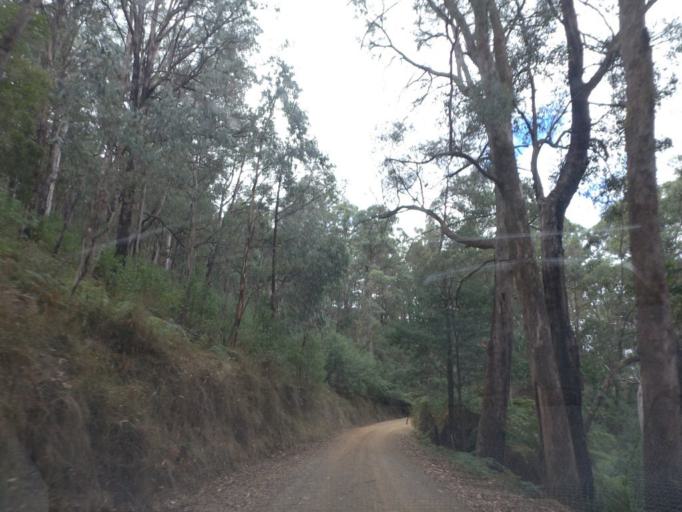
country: AU
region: Victoria
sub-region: Murrindindi
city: Alexandra
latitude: -37.4316
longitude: 145.9709
